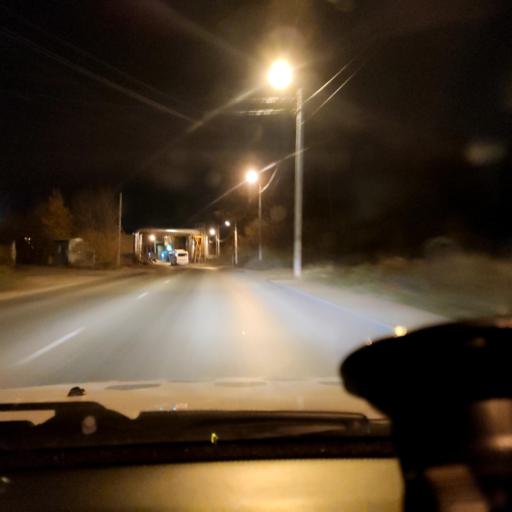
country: RU
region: Perm
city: Kondratovo
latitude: 57.9516
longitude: 56.1379
